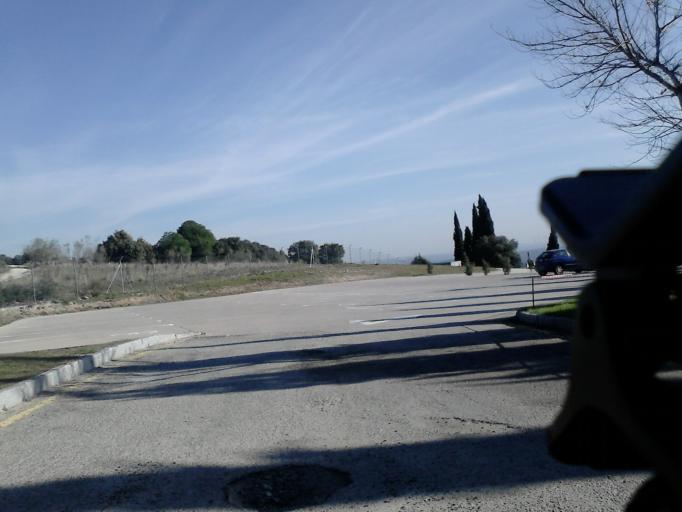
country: ES
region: Madrid
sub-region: Provincia de Madrid
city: Torrelodones
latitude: 40.5734
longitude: -3.9206
